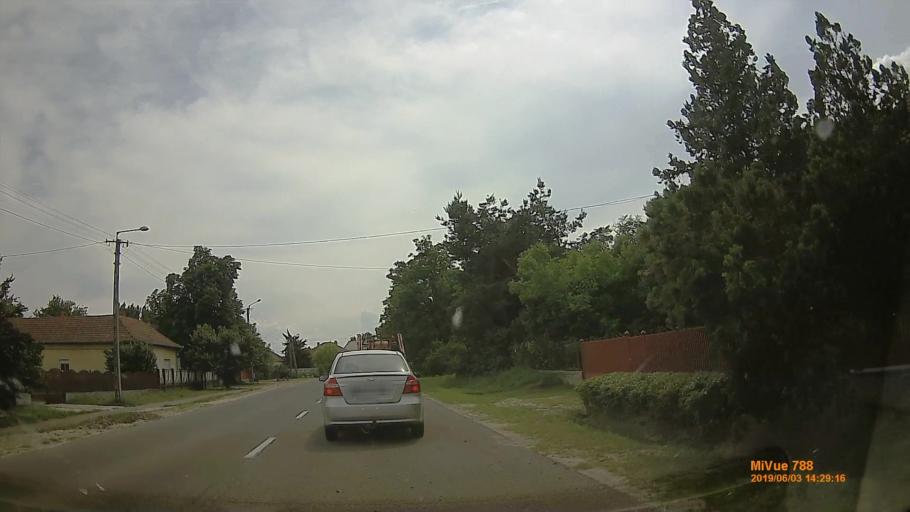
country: HU
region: Bacs-Kiskun
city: Tiszakecske
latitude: 46.9728
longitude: 20.1109
